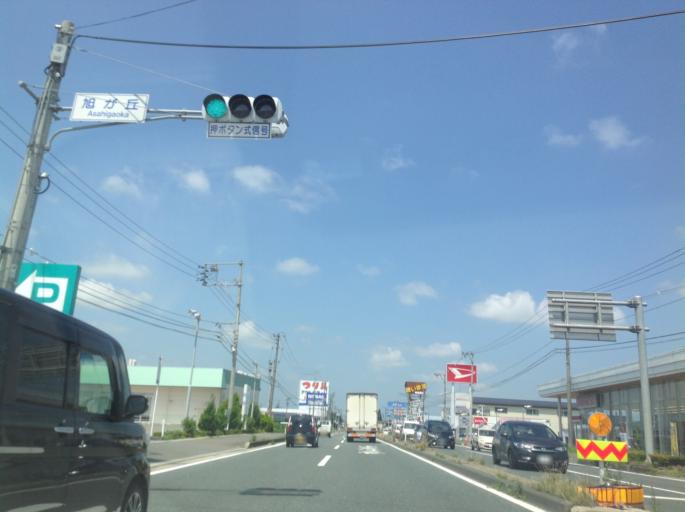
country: JP
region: Iwate
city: Kitakami
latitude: 39.3151
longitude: 141.1126
